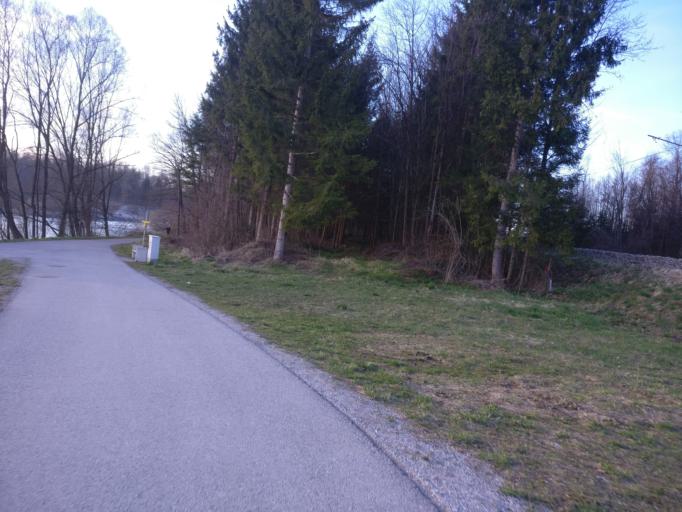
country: DE
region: Bavaria
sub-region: Upper Bavaria
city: Freilassing
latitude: 47.8505
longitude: 13.0073
